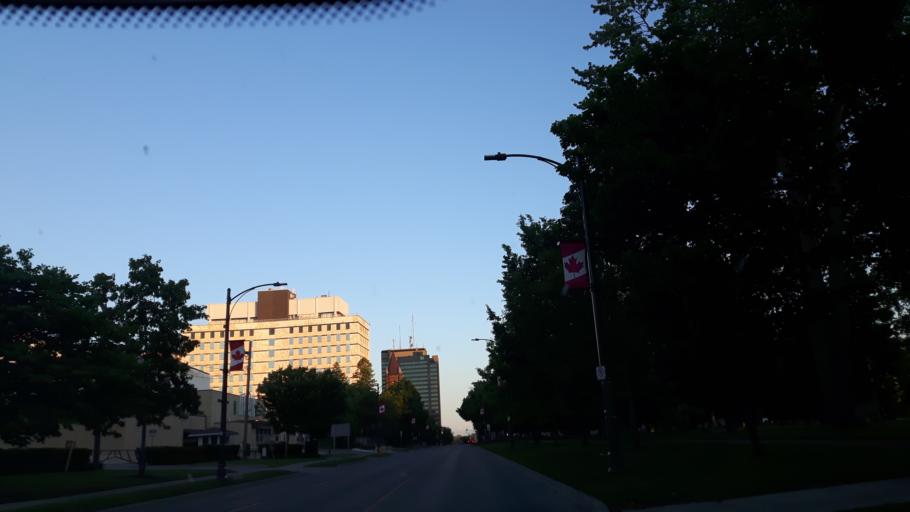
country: CA
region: Ontario
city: London
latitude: 42.9900
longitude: -81.2479
